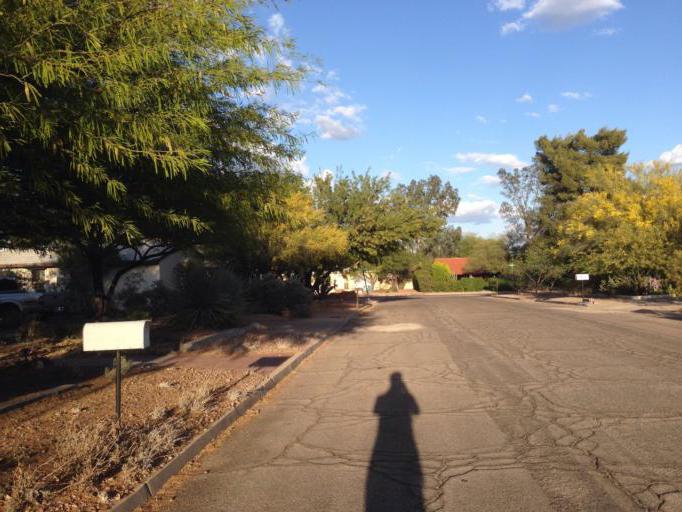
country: US
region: Arizona
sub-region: Pima County
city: Tucson
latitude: 32.2475
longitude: -110.9376
